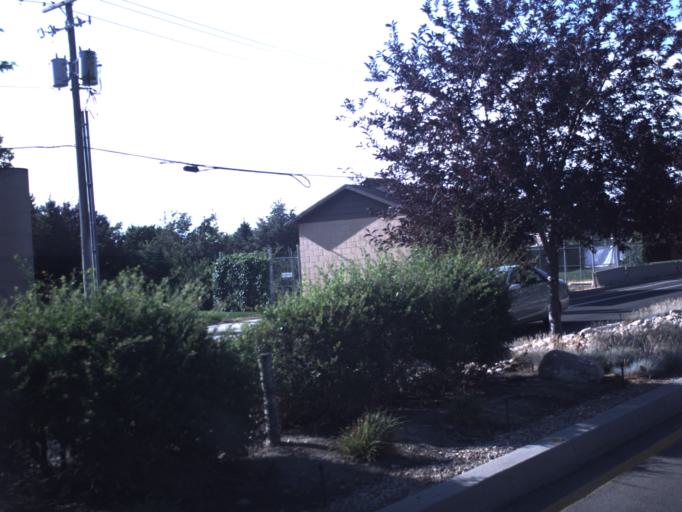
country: US
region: Utah
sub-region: Utah County
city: Cedar Hills
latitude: 40.4154
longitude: -111.7880
